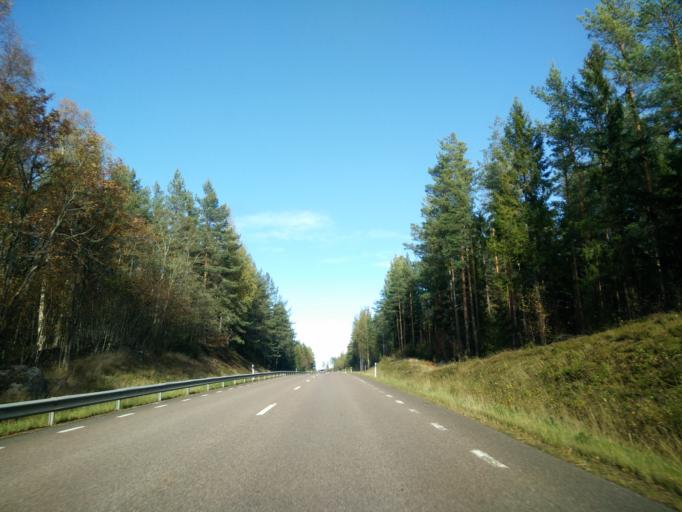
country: SE
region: Gaevleborg
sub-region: Hudiksvalls Kommun
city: Iggesund
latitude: 61.5544
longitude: 17.0088
